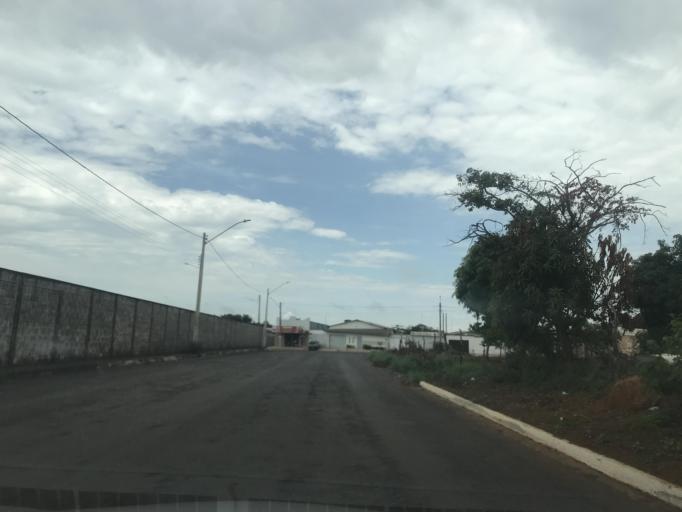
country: BR
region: Goias
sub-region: Luziania
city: Luziania
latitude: -16.2579
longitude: -47.9747
